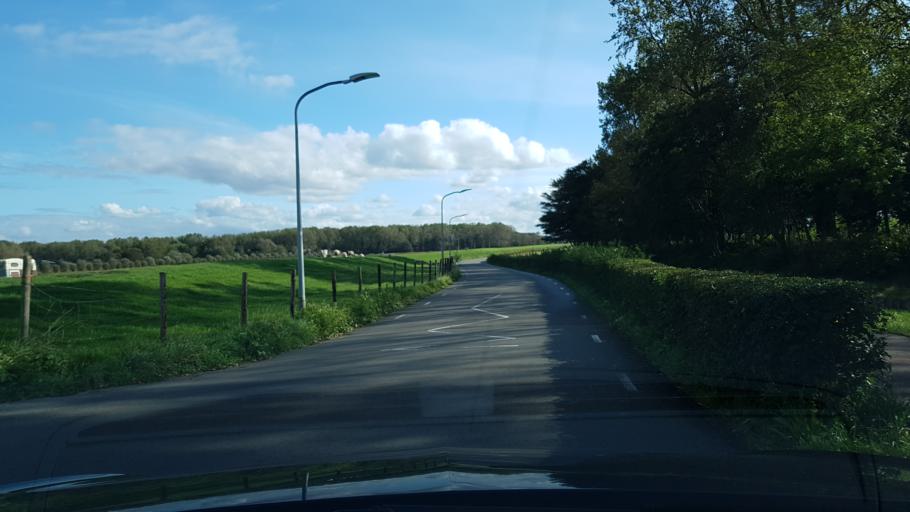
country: NL
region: North Holland
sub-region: Gemeente Velsen
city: Velsen-Zuid
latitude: 52.4244
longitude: 4.6637
